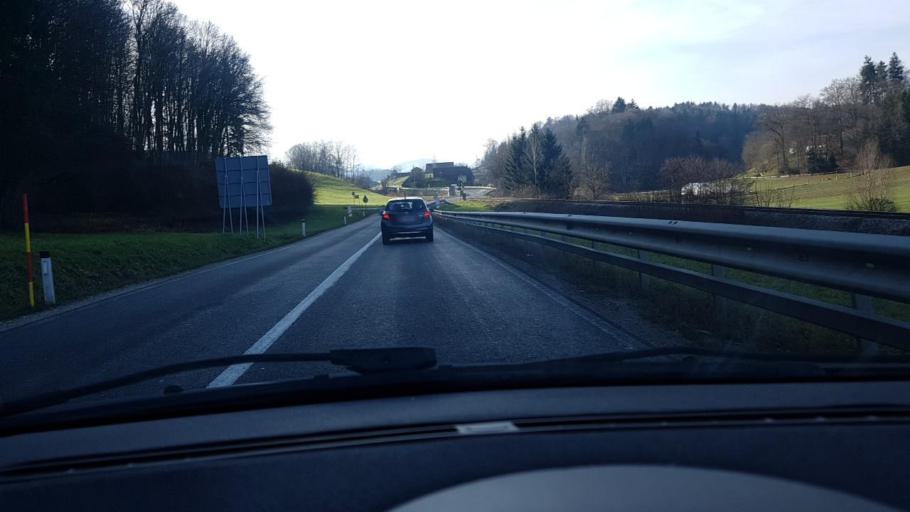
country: SI
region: Smarje pri Jelsah
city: Smarje pri Jelsah
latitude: 46.2294
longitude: 15.4753
